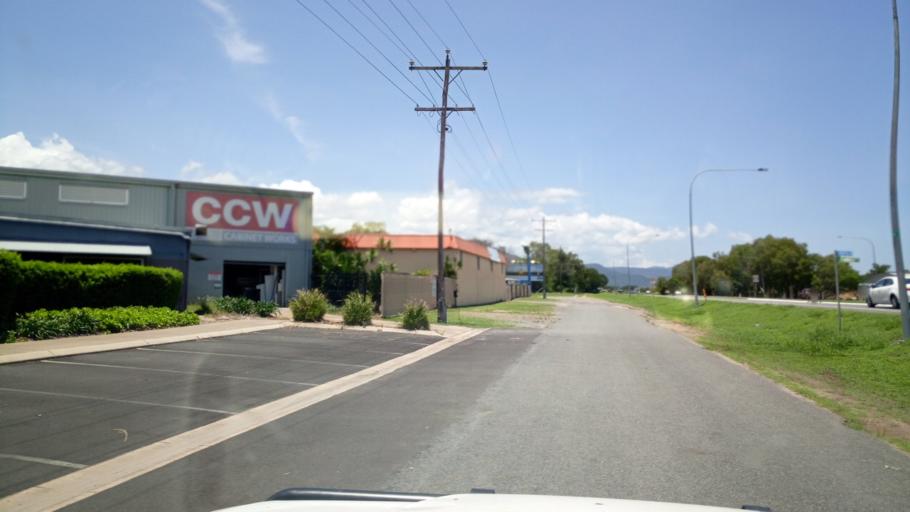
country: AU
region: Queensland
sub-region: Cairns
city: Redlynch
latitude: -16.8722
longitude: 145.7393
